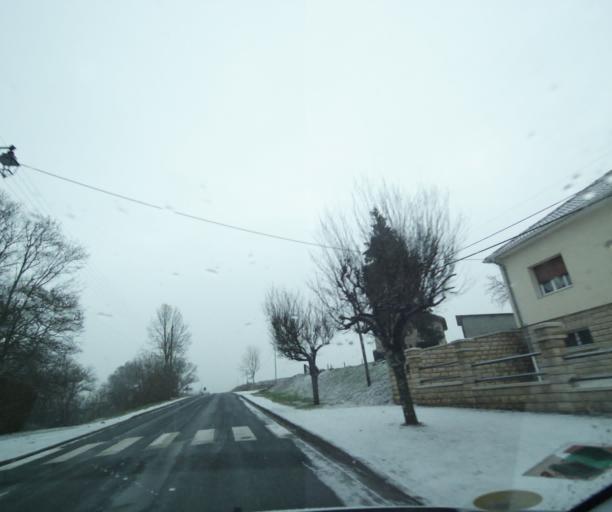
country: FR
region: Champagne-Ardenne
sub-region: Departement de la Haute-Marne
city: Wassy
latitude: 48.4887
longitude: 4.9733
